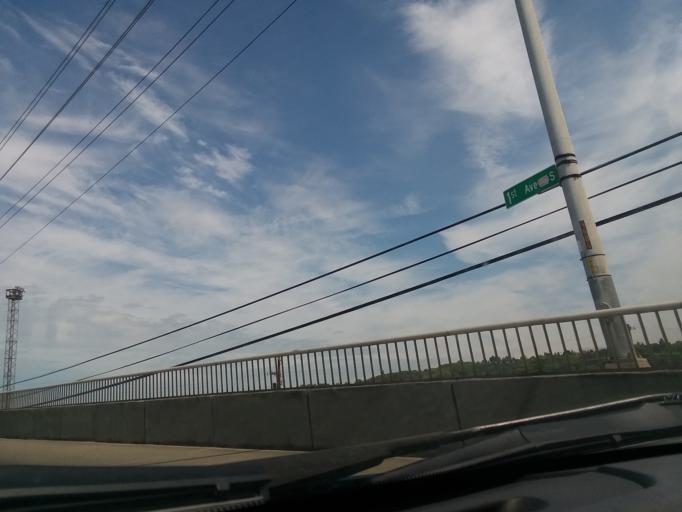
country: US
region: Washington
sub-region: King County
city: Seattle
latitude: 47.5614
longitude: -122.3340
